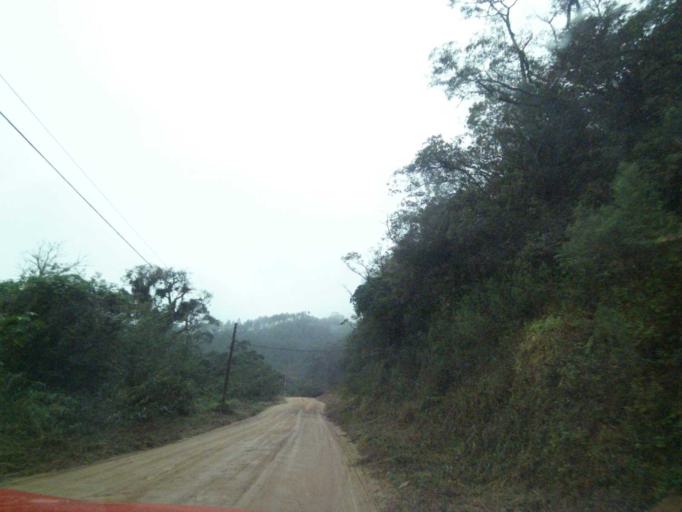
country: BR
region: Santa Catarina
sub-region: Anitapolis
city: Anitapolis
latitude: -27.9166
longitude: -49.1333
